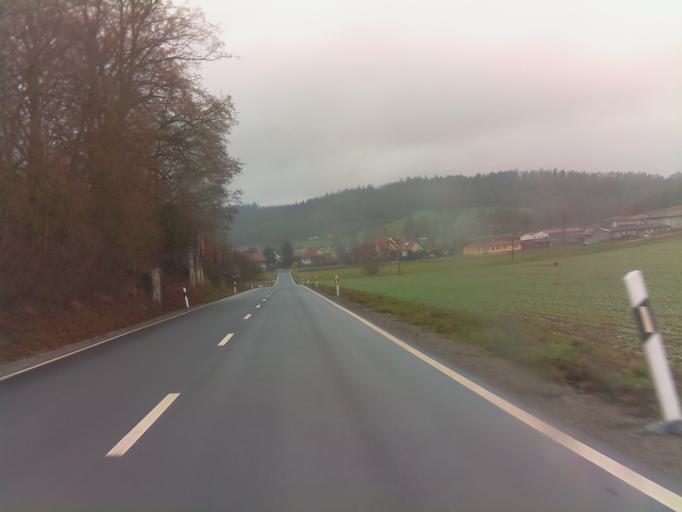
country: DE
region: Thuringia
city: Juchsen
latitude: 50.4498
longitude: 10.5443
